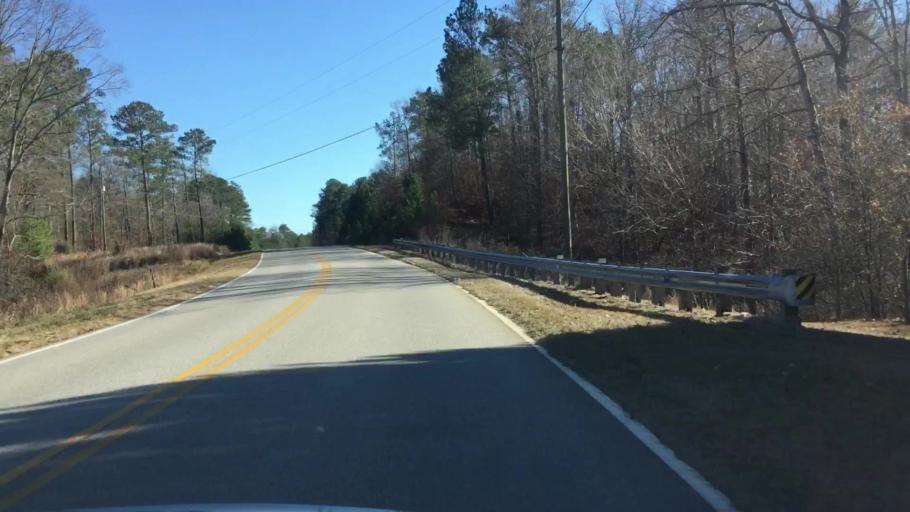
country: US
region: Georgia
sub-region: Newton County
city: Oakwood
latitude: 33.4859
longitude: -84.0442
